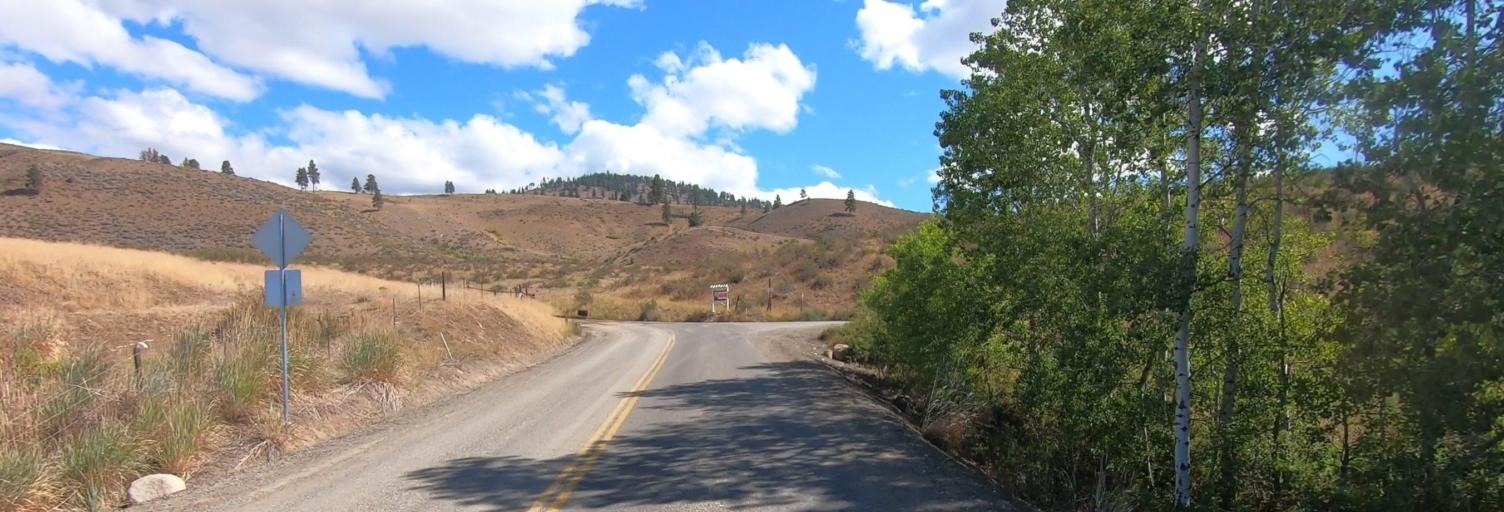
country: US
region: Washington
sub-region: Okanogan County
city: Brewster
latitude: 48.5002
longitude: -120.1496
